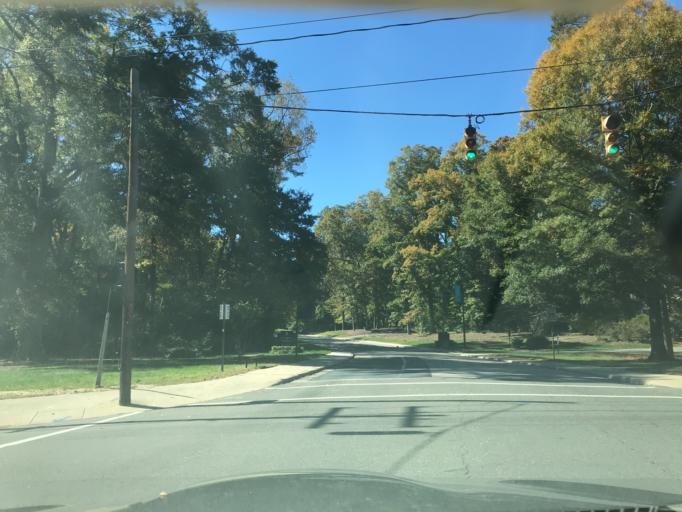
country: US
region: North Carolina
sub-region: Durham County
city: Durham
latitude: 36.0000
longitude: -78.9301
